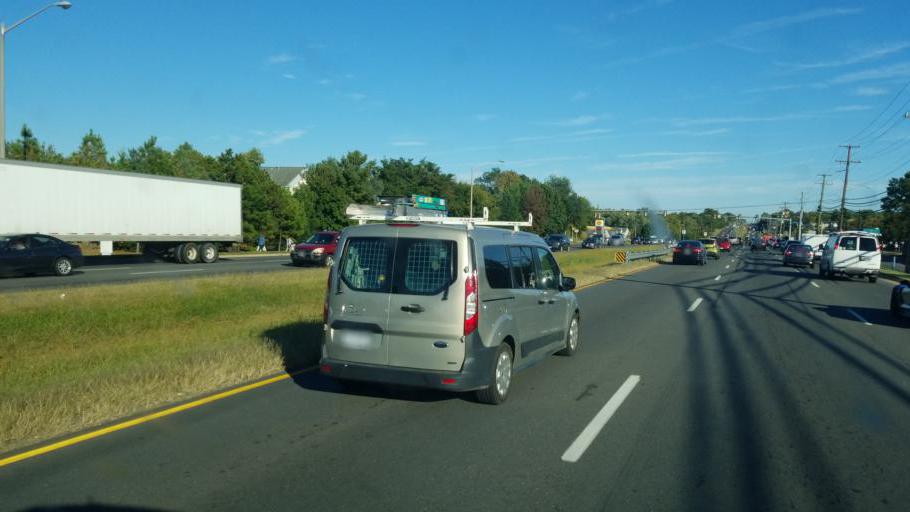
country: US
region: Virginia
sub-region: Fairfax County
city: Chantilly
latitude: 38.8914
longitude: -77.4244
